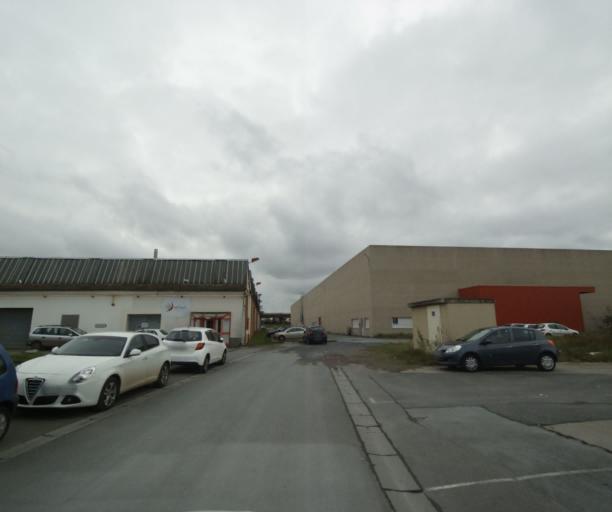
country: FR
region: Pays de la Loire
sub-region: Departement de la Sarthe
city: Le Mans
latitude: 47.9822
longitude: 0.2028
